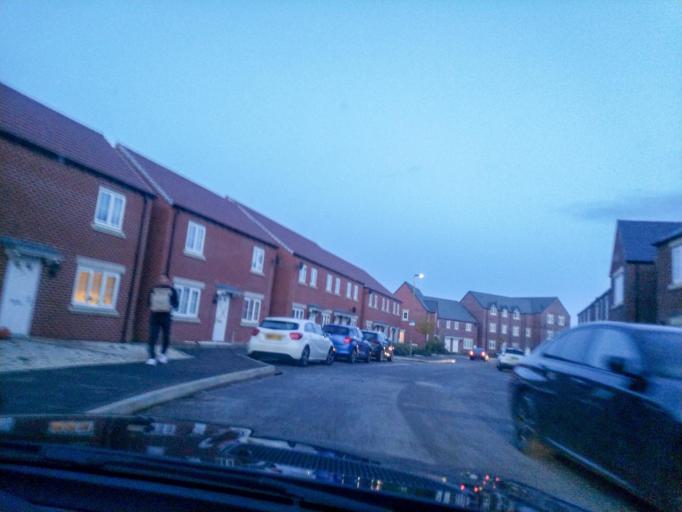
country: GB
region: England
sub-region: Oxfordshire
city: Banbury
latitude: 52.0425
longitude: -1.3248
